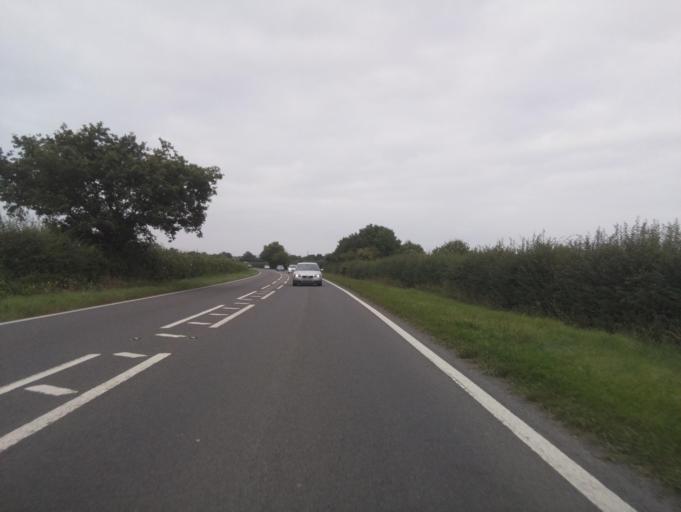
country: GB
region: England
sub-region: Shropshire
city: Shawbury
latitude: 52.7778
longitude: -2.6641
